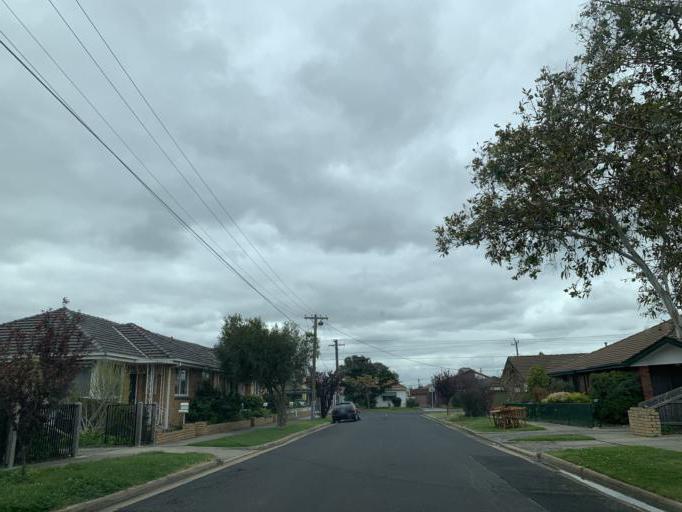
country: AU
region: Victoria
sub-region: Moreland
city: Pascoe Vale South
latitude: -37.7306
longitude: 144.9453
